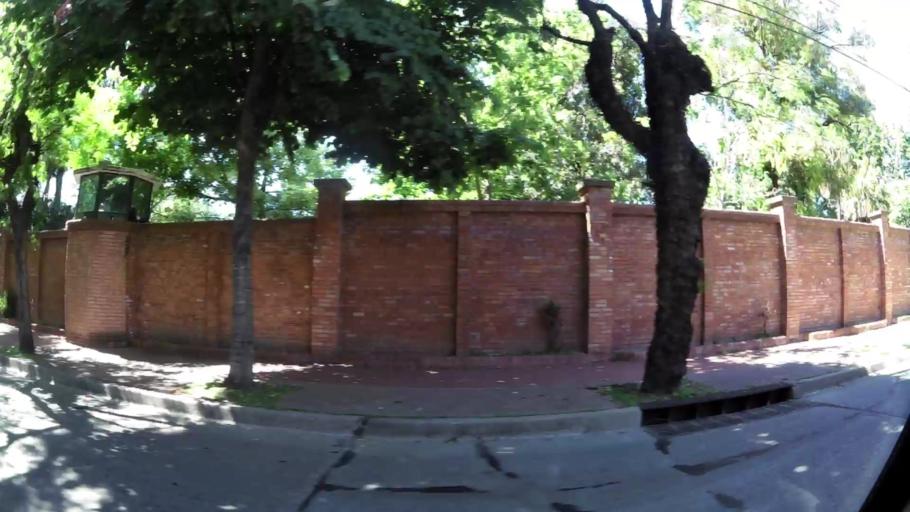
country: AR
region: Buenos Aires
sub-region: Partido de Vicente Lopez
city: Olivos
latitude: -34.5142
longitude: -58.4846
